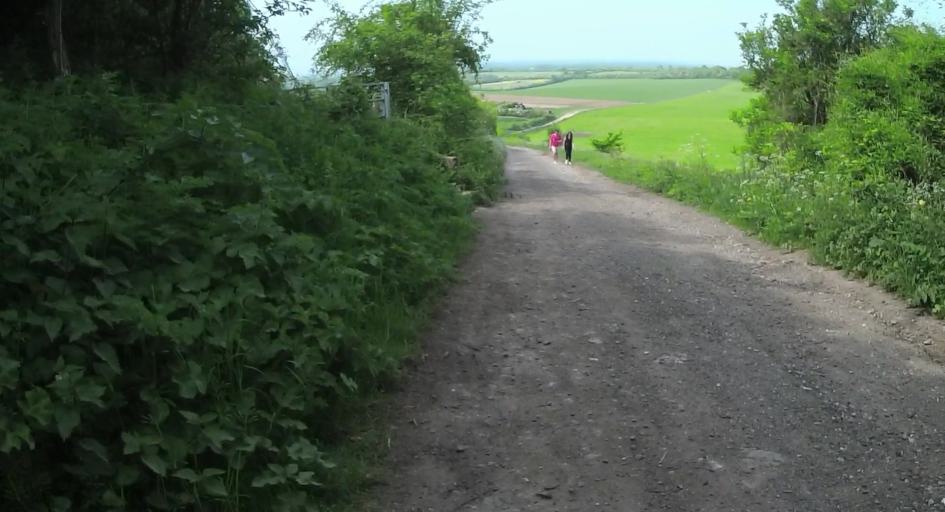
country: GB
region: England
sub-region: Hampshire
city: Kingsclere
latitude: 51.3101
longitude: -1.2302
